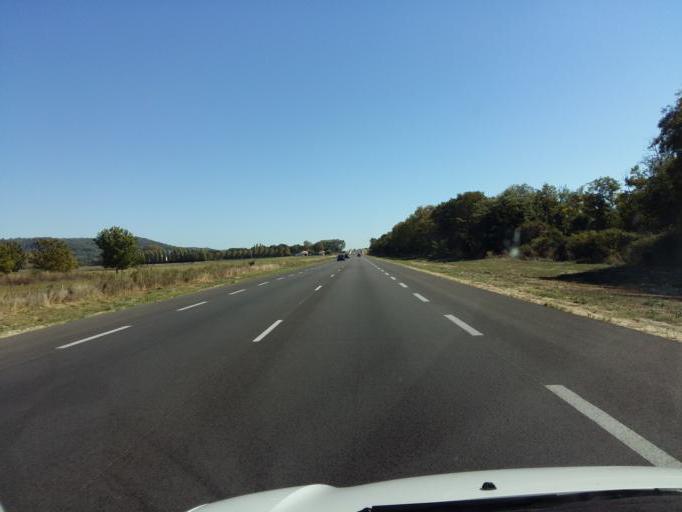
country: FR
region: Provence-Alpes-Cote d'Azur
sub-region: Departement du Vaucluse
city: Villelaure
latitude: 43.7165
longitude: 5.4029
